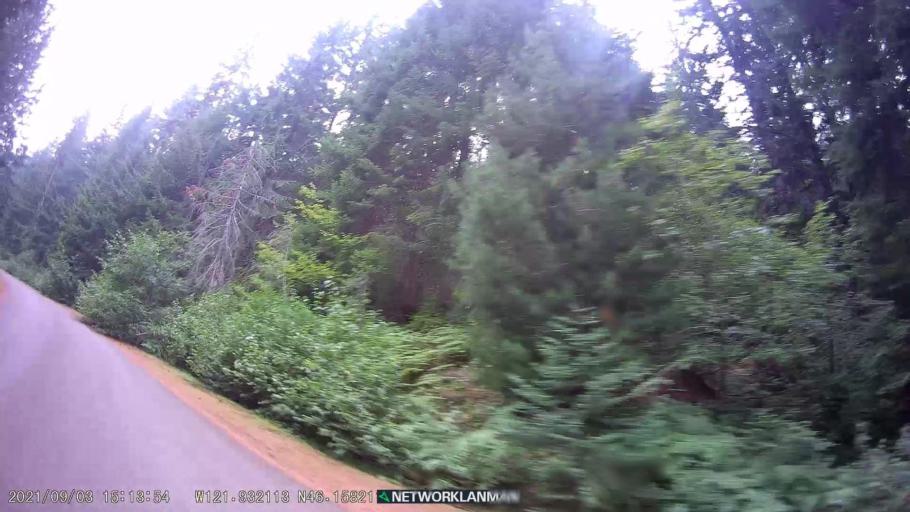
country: US
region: Washington
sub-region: Skamania County
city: Carson
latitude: 46.1581
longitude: -121.9322
